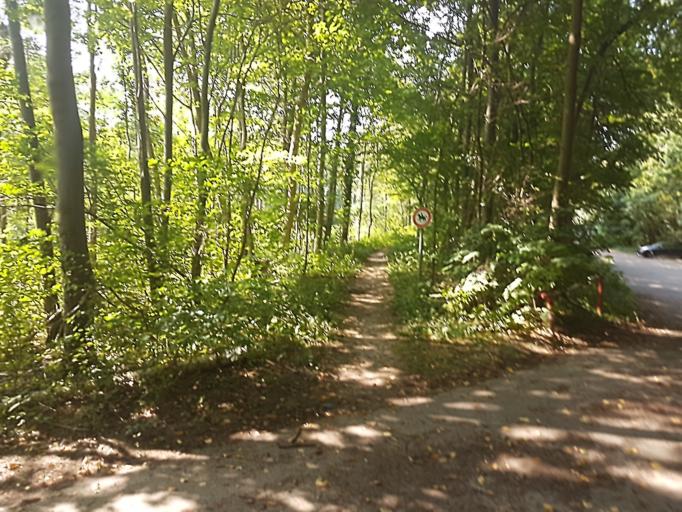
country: DE
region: Rheinland-Pfalz
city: Otterstadt
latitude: 49.3732
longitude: 8.4885
